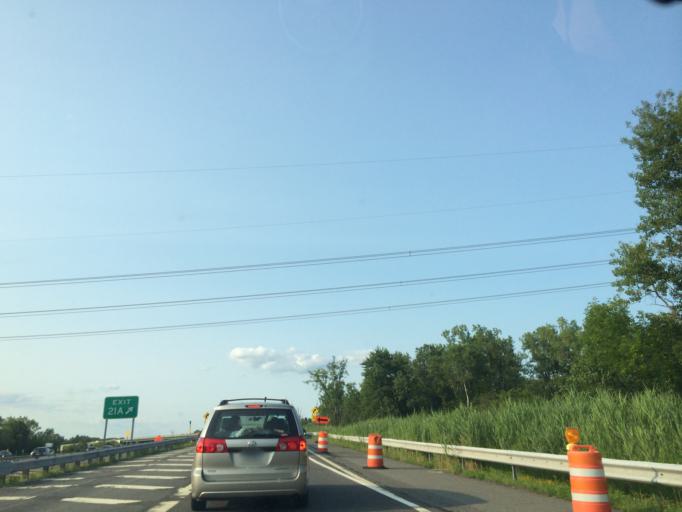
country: US
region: New York
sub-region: Rensselaer County
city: Castleton-on-Hudson
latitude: 42.5117
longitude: -73.7900
